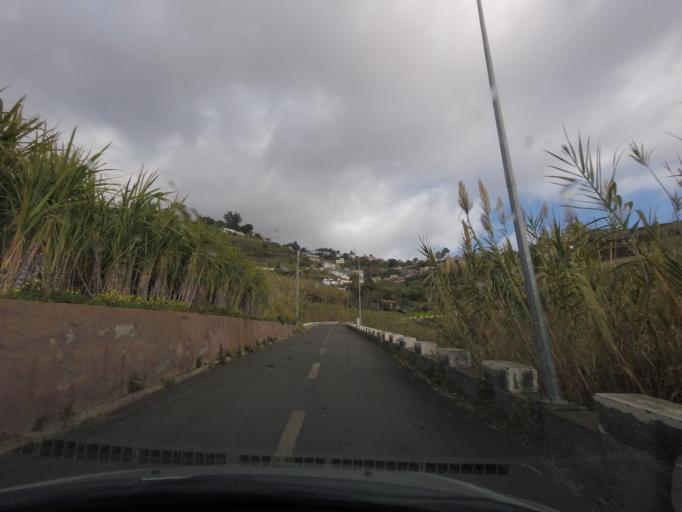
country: PT
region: Madeira
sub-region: Ribeira Brava
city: Campanario
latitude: 32.6628
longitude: -17.0235
